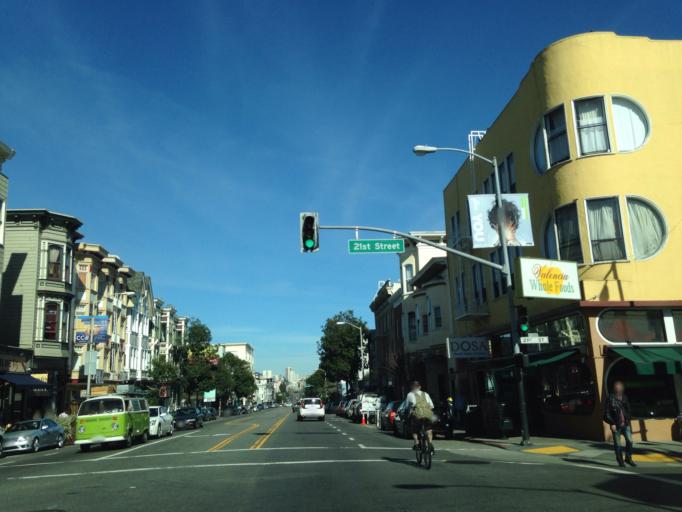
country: US
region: California
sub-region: San Francisco County
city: San Francisco
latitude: 37.7568
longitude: -122.4211
